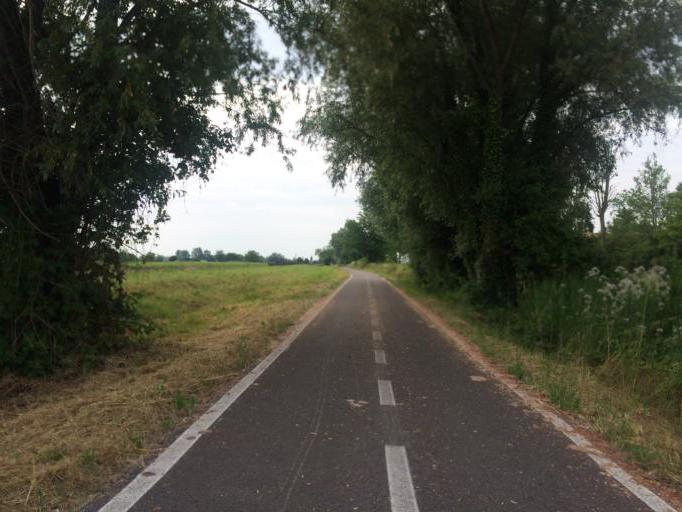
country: IT
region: Friuli Venezia Giulia
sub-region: Provincia di Udine
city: Aquileia
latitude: 45.7623
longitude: 13.3727
